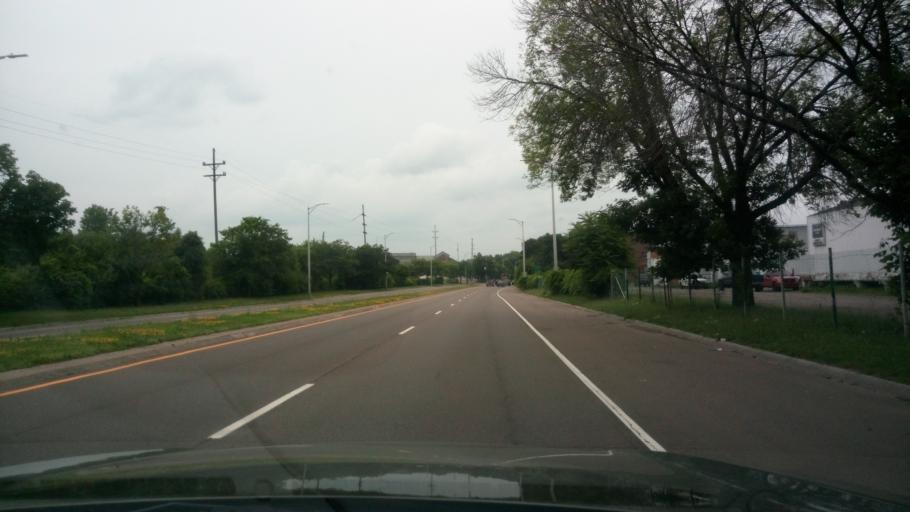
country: US
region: New York
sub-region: Chemung County
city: Elmira
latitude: 42.0945
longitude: -76.8069
